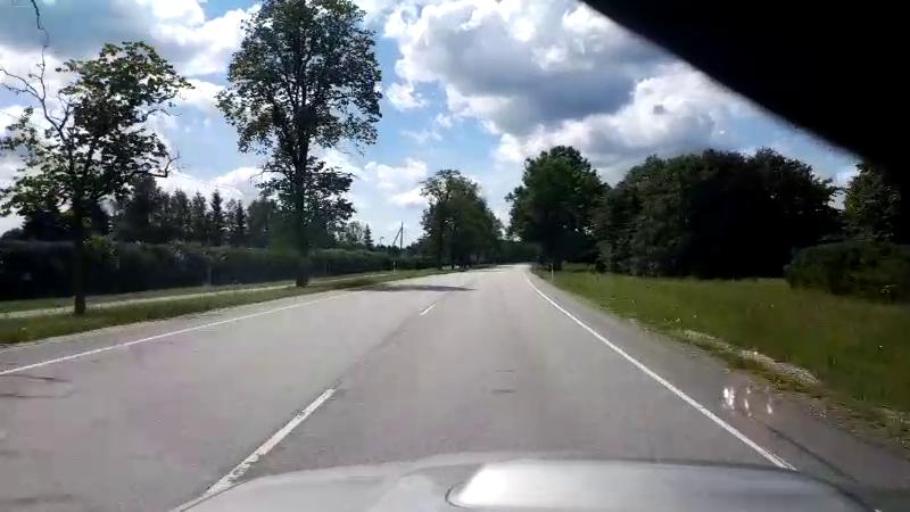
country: EE
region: Jaervamaa
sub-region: Jaerva-Jaani vald
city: Jarva-Jaani
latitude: 59.0379
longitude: 25.7078
